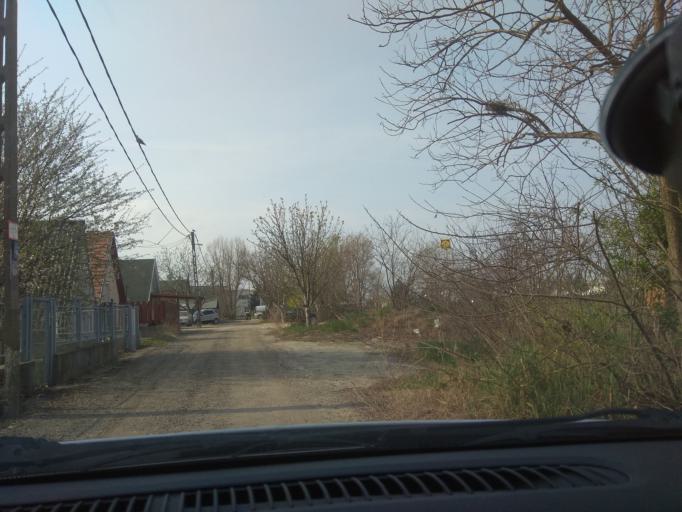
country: HU
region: Pest
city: Szigetszentmiklos
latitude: 47.3763
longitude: 19.0510
